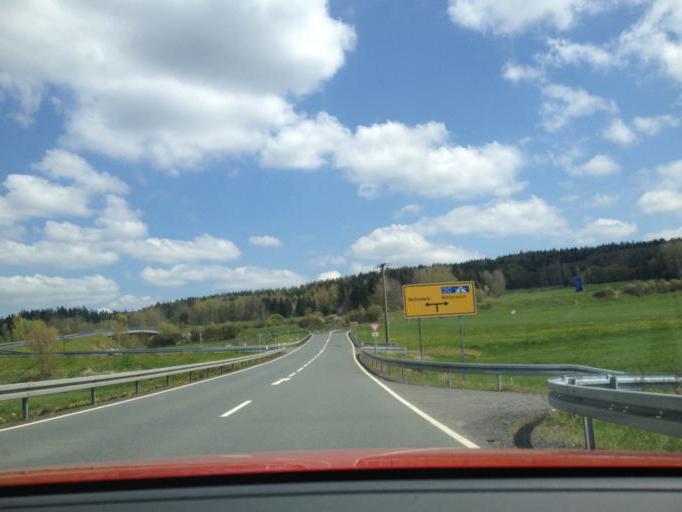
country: DE
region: Bavaria
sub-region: Upper Palatinate
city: Pechbrunn
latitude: 49.9840
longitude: 12.1265
